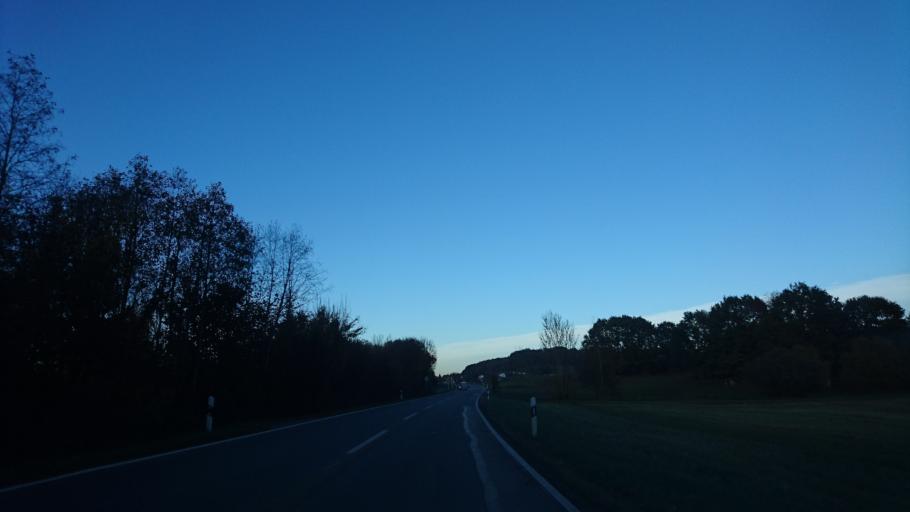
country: DE
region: Bavaria
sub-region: Swabia
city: Dinkelscherben
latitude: 48.3593
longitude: 10.5719
